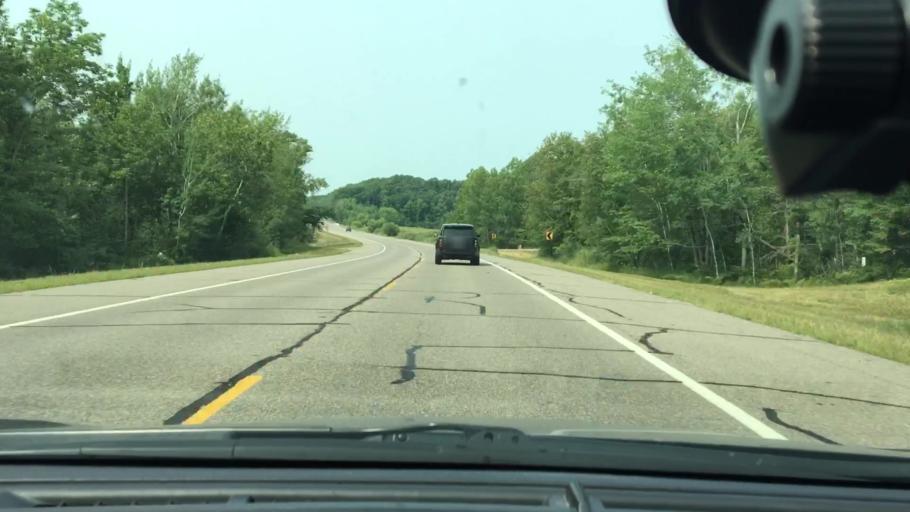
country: US
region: Minnesota
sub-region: Crow Wing County
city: Baxter
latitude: 46.3840
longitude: -94.3092
